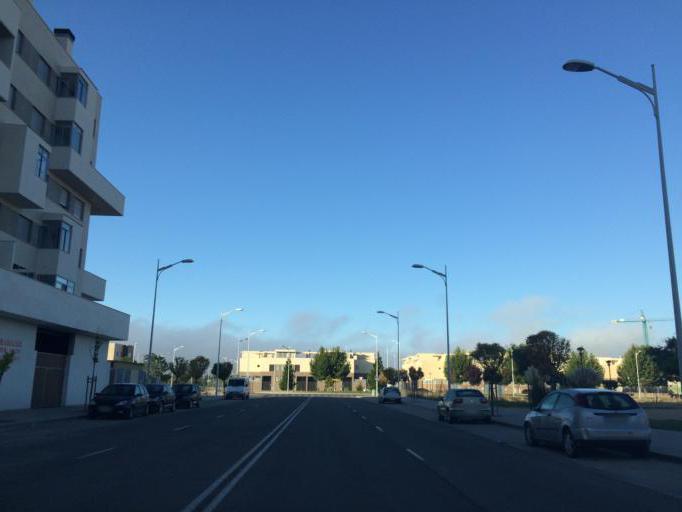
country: ES
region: Castille-La Mancha
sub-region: Provincia de Albacete
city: Albacete
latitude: 39.0061
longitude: -1.8760
